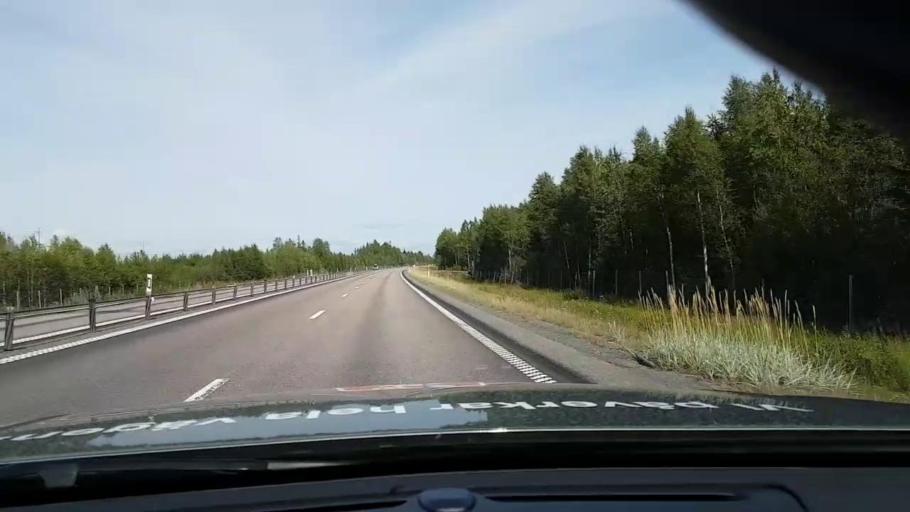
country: SE
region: Vaesternorrland
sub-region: OErnskoeldsviks Kommun
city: Husum
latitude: 63.4435
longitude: 19.2163
